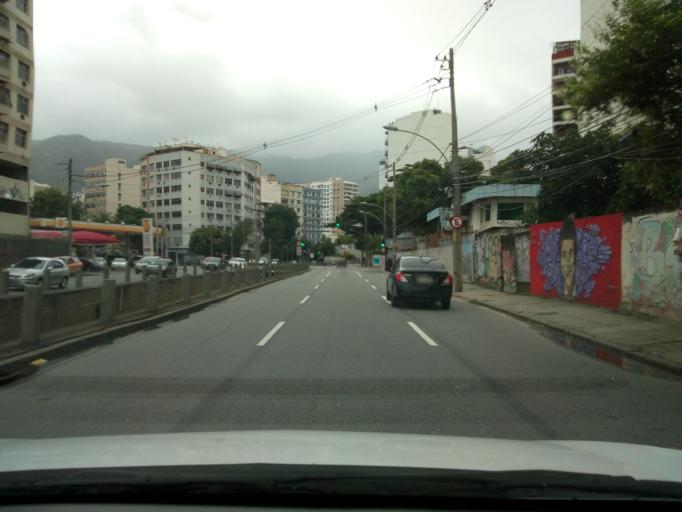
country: BR
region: Rio de Janeiro
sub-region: Rio De Janeiro
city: Rio de Janeiro
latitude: -22.9129
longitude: -43.2341
